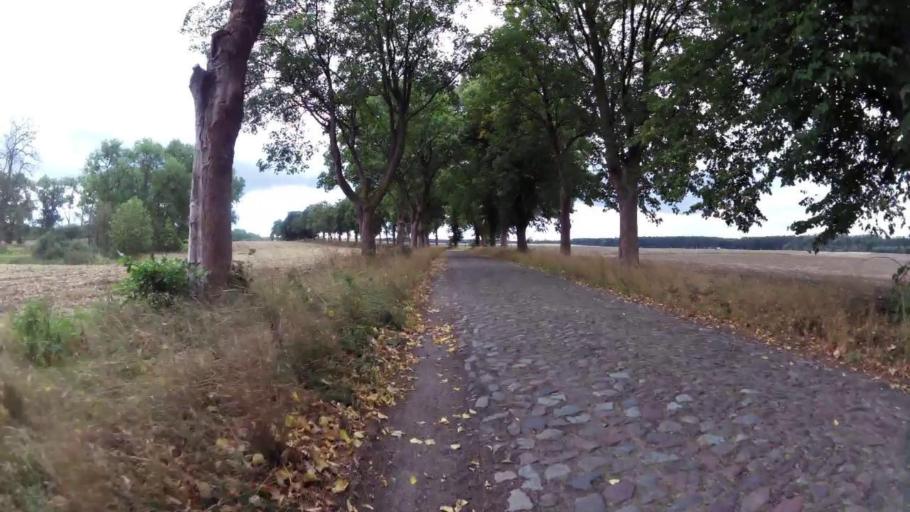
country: PL
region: West Pomeranian Voivodeship
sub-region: Powiat mysliborski
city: Debno
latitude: 52.8406
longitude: 14.7127
